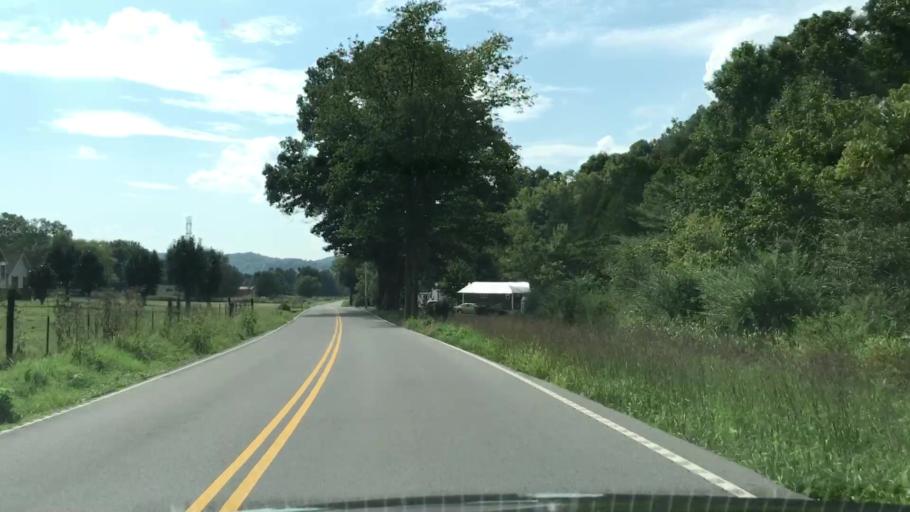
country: US
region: Tennessee
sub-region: Trousdale County
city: Hartsville
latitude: 36.4794
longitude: -86.1855
